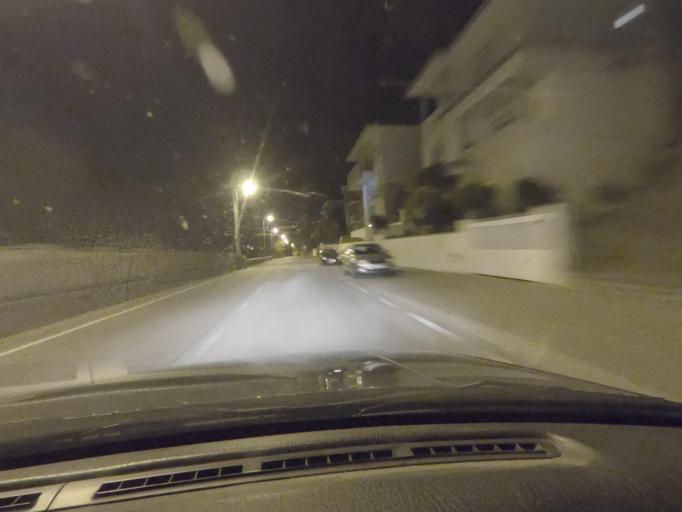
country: PT
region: Vila Real
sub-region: Peso da Regua
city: Godim
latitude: 41.1750
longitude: -7.7958
